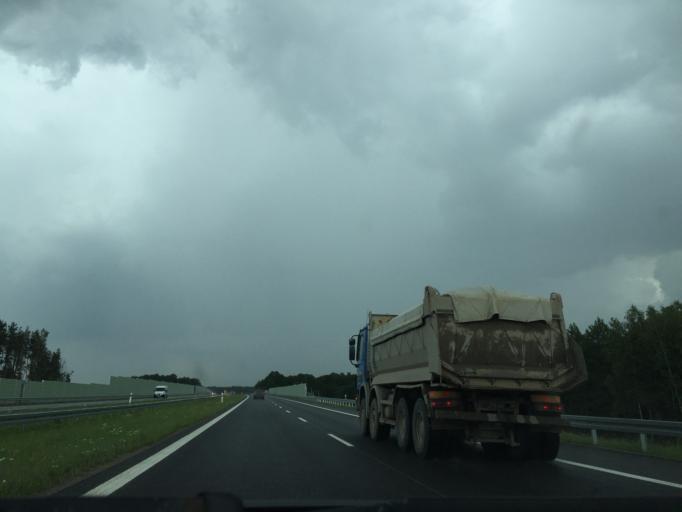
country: PL
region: Masovian Voivodeship
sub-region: Powiat szydlowiecki
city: Oronsko
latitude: 51.3073
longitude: 21.0051
